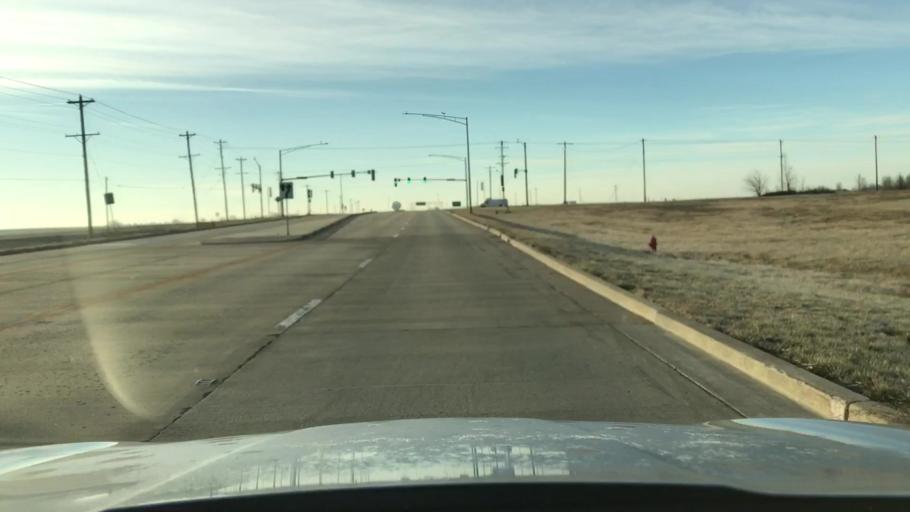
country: US
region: Illinois
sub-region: McLean County
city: Normal
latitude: 40.5486
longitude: -88.9444
